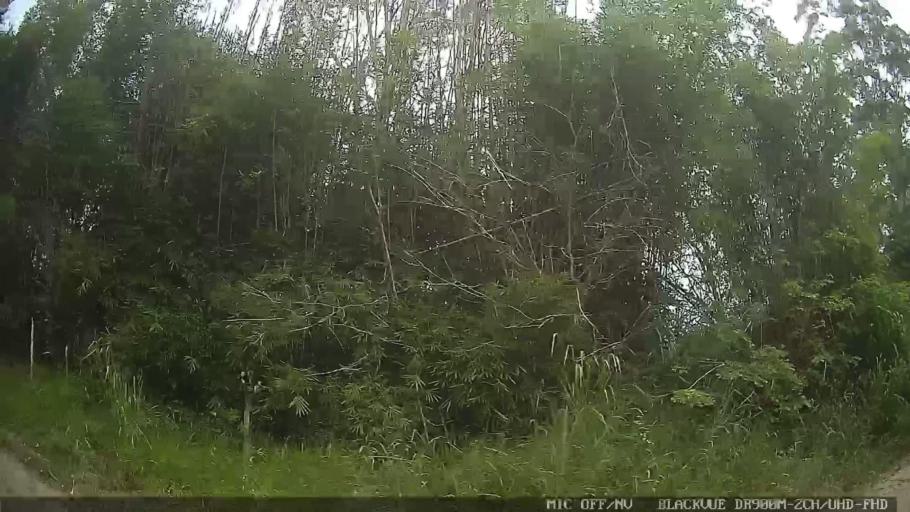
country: BR
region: Sao Paulo
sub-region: Mogi das Cruzes
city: Mogi das Cruzes
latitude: -23.4345
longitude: -46.2282
